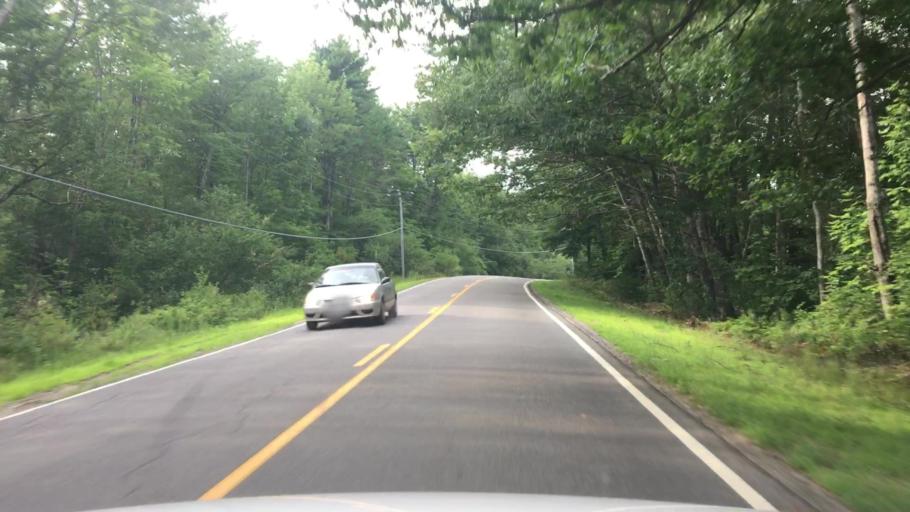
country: US
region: Maine
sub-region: Knox County
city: Washington
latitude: 44.2796
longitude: -69.3683
